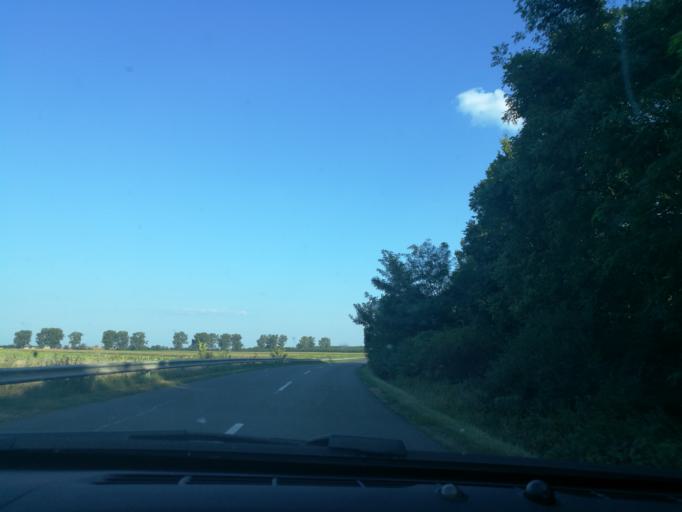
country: HU
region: Szabolcs-Szatmar-Bereg
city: Tiszabercel
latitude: 48.1441
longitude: 21.6376
